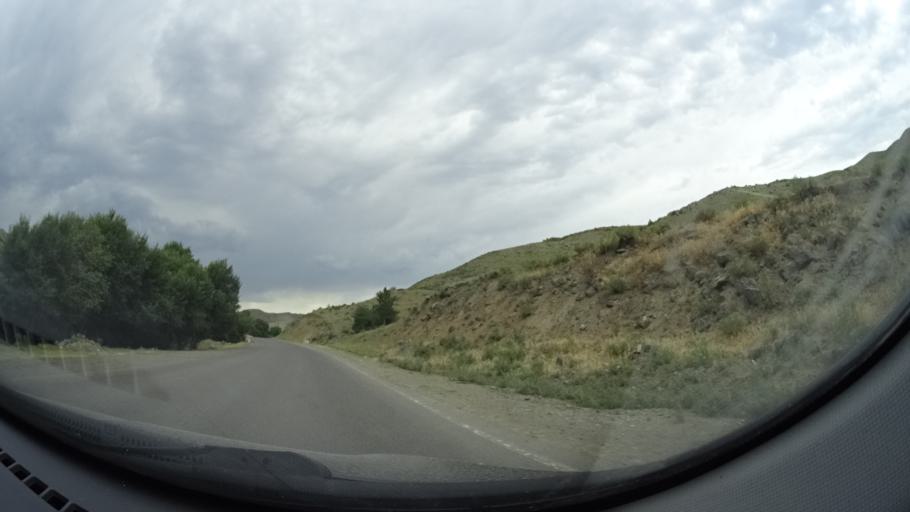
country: GE
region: Samtskhe-Javakheti
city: Aspindza
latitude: 41.5964
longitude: 43.1552
